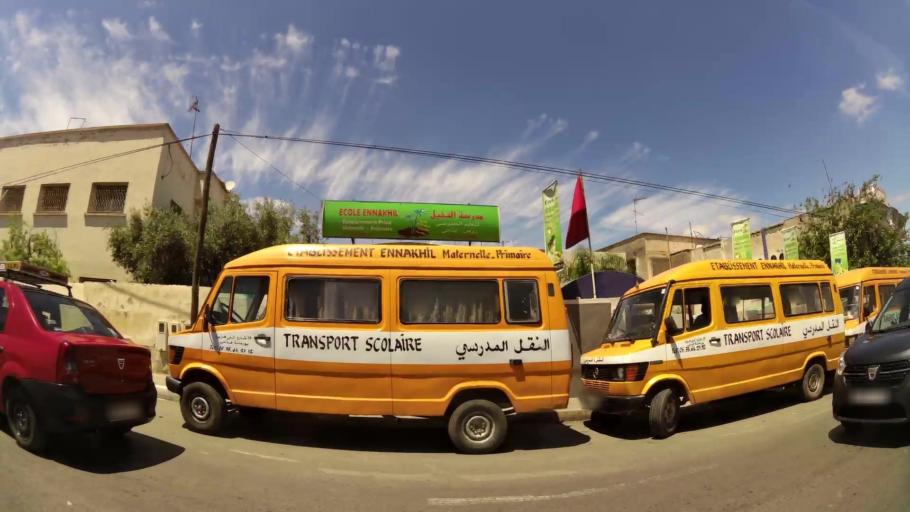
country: MA
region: Fes-Boulemane
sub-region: Fes
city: Fes
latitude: 34.0171
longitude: -4.9904
